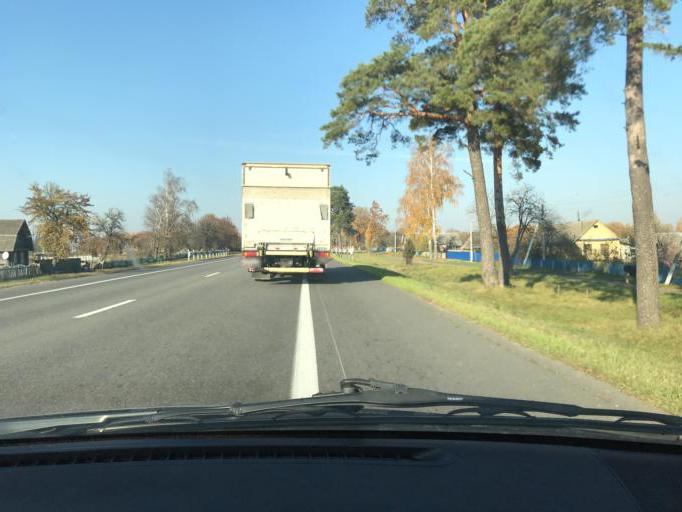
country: BY
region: Vitebsk
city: Balbasava
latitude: 54.3296
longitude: 30.4467
